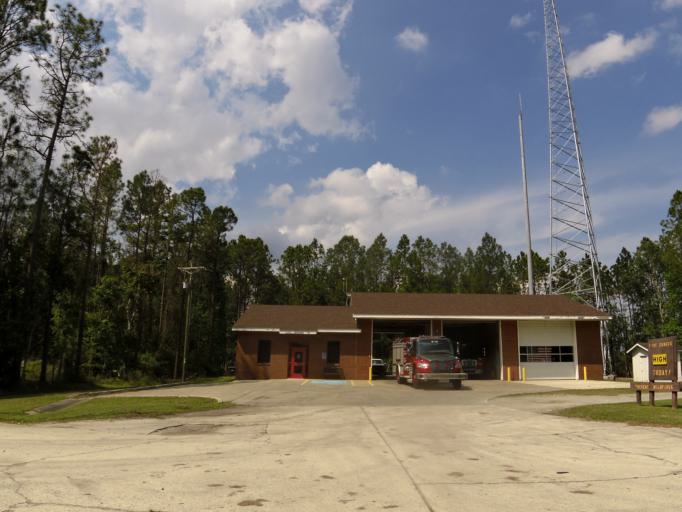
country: US
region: Georgia
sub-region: Camden County
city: Kingsland
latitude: 30.8091
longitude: -81.8013
